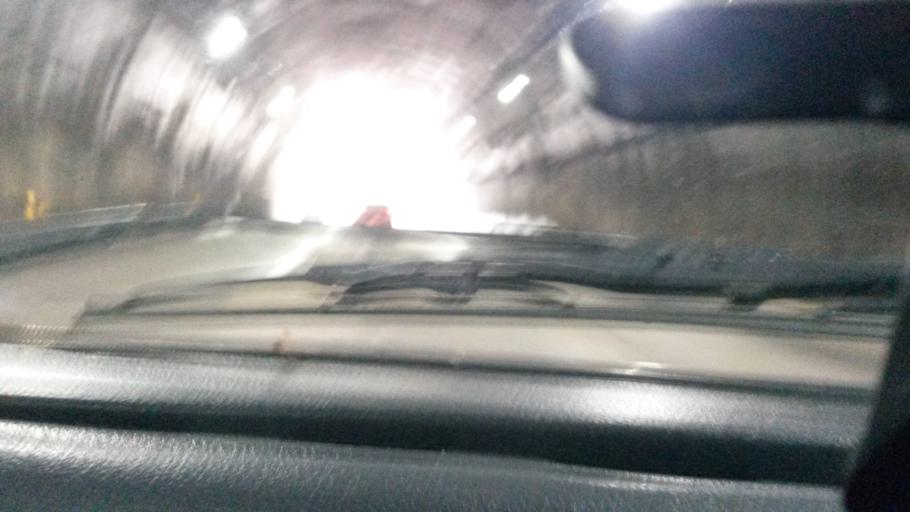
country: BR
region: Sao Paulo
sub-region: Cubatao
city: Cubatao
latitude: -23.9104
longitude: -46.5184
